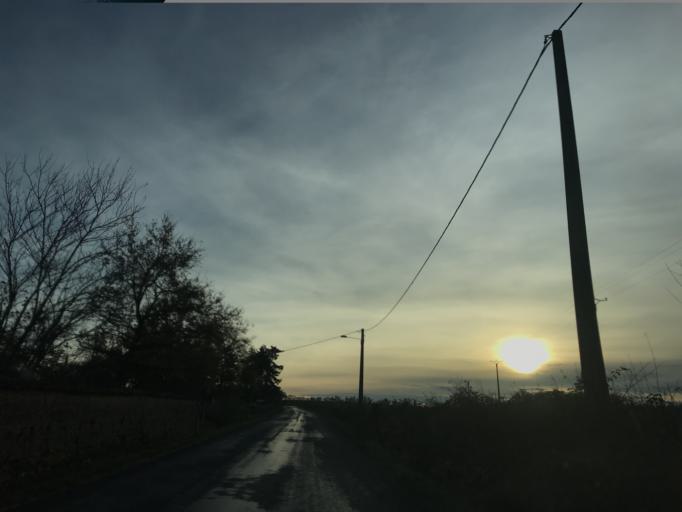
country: FR
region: Auvergne
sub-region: Departement du Puy-de-Dome
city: Courpiere
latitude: 45.7632
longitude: 3.5825
